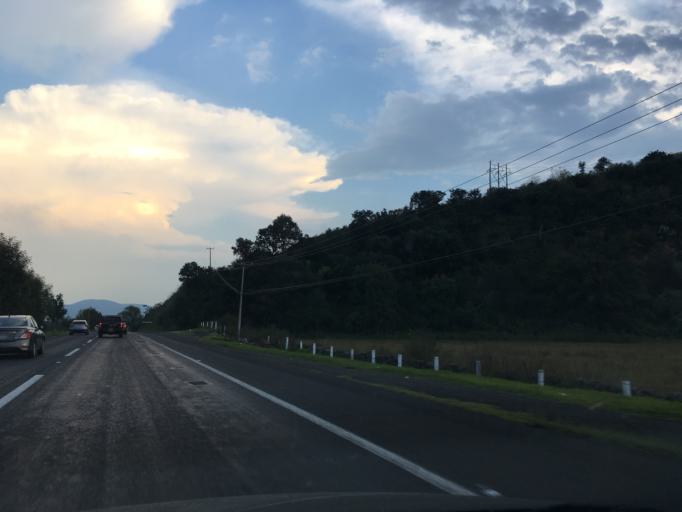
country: MX
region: Michoacan
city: Lagunillas
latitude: 19.5596
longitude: -101.4023
